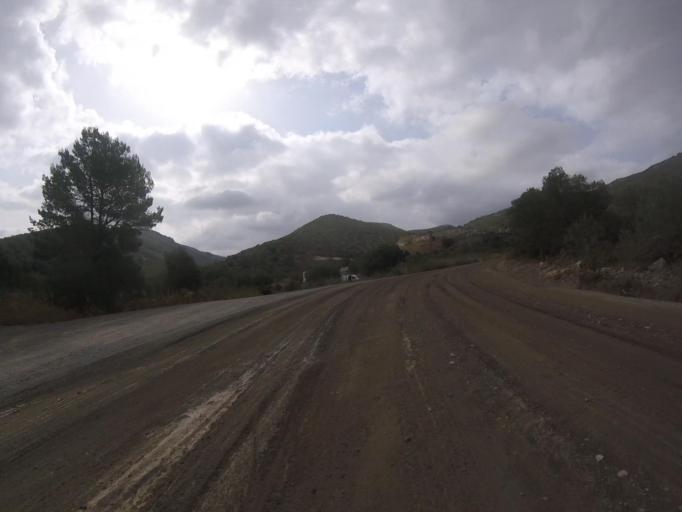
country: ES
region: Valencia
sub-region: Provincia de Castello
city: Santa Magdalena de Pulpis
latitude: 40.3500
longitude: 0.3059
